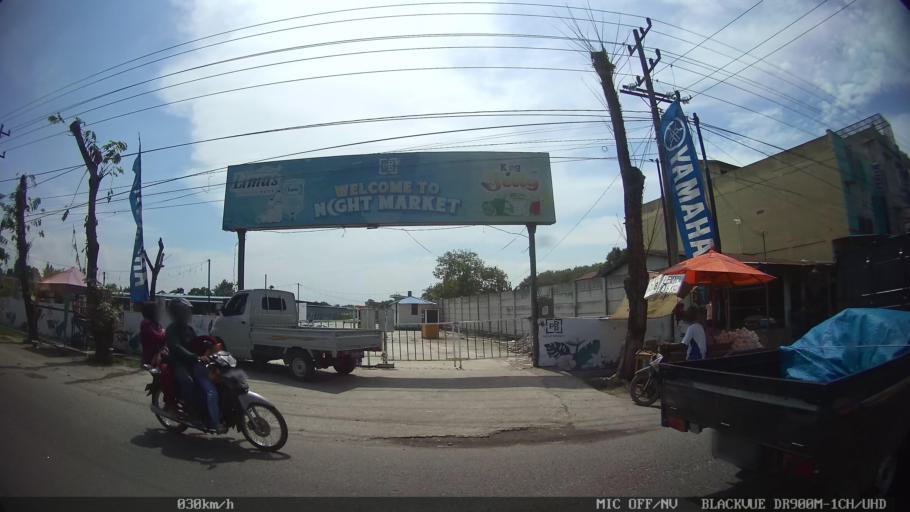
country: ID
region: North Sumatra
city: Labuhan Deli
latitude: 3.6774
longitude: 98.6559
